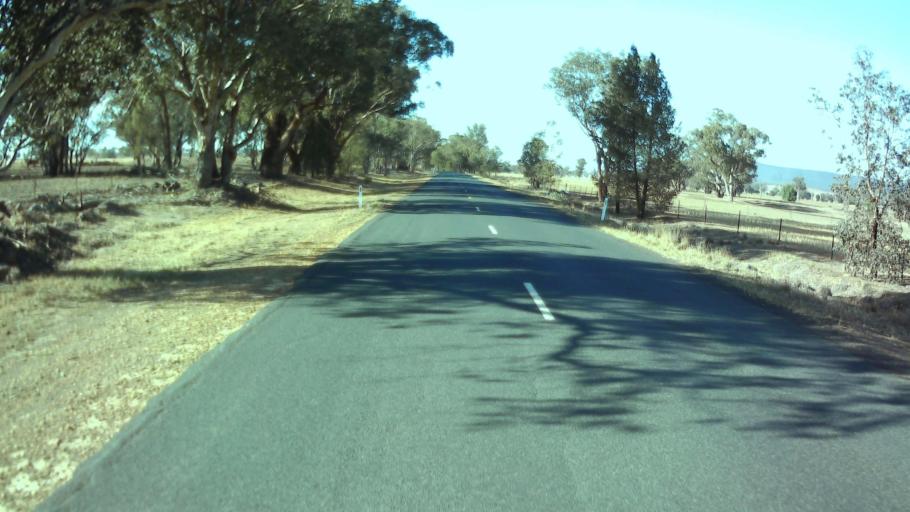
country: AU
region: New South Wales
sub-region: Weddin
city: Grenfell
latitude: -33.9270
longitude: 148.1381
